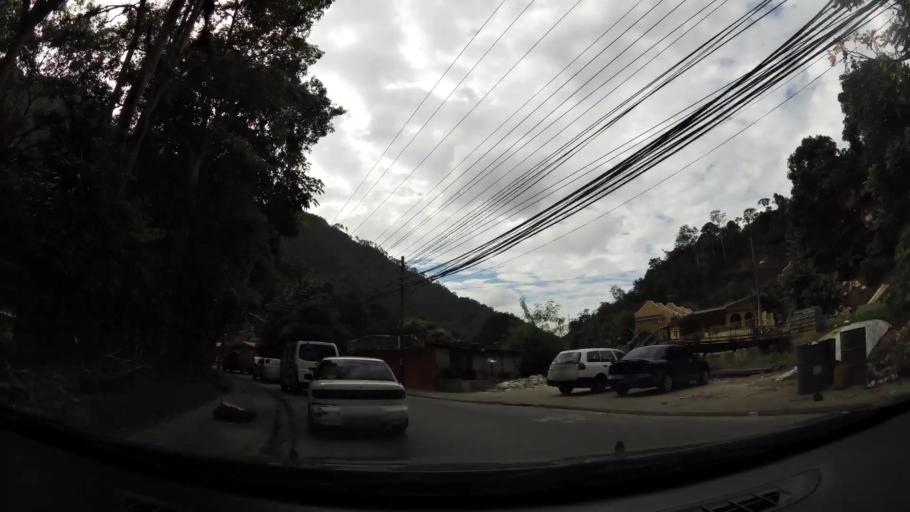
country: TT
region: Diego Martin
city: Petit Valley
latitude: 10.7054
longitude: -61.5120
